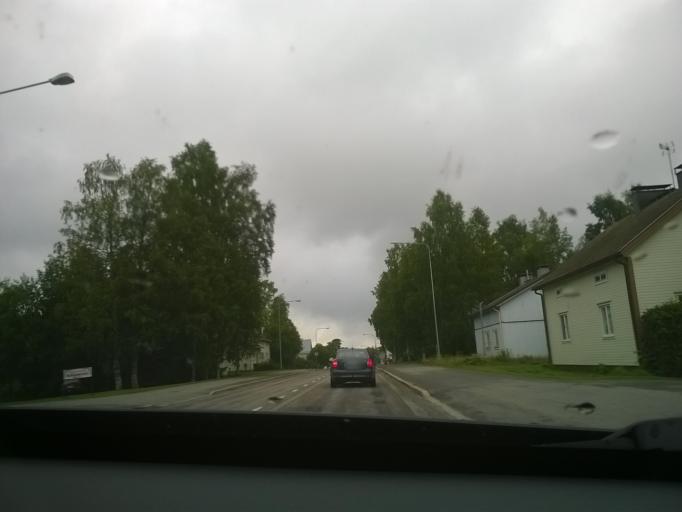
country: FI
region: Kainuu
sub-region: Kehys-Kainuu
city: Kuhmo
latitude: 64.1251
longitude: 29.5132
